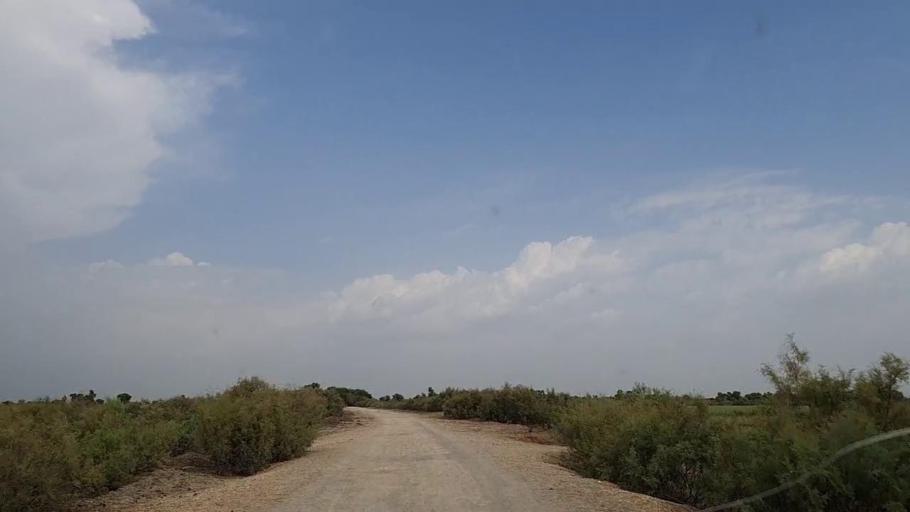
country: PK
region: Sindh
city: Khanpur
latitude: 27.8190
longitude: 69.5304
